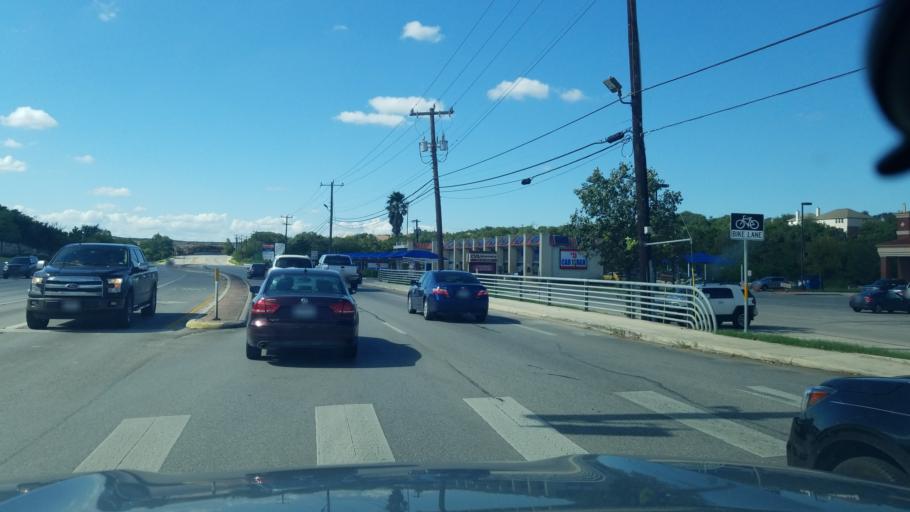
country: US
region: Texas
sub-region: Bexar County
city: Hollywood Park
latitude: 29.6213
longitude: -98.5131
